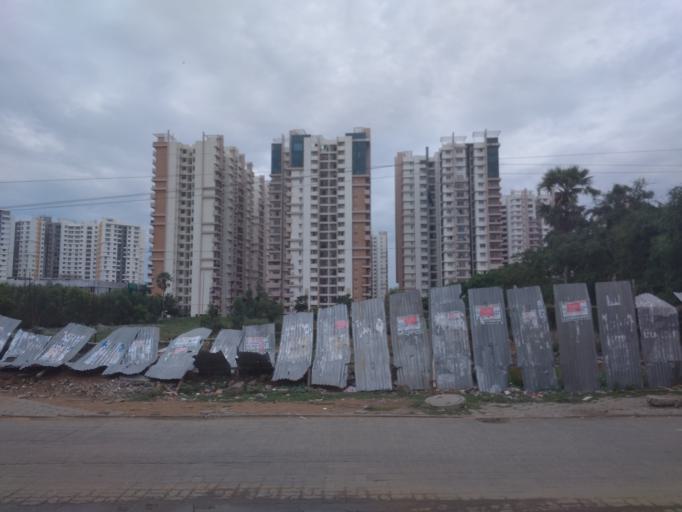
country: IN
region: Tamil Nadu
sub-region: Kancheepuram
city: Injambakkam
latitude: 12.8496
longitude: 80.2267
